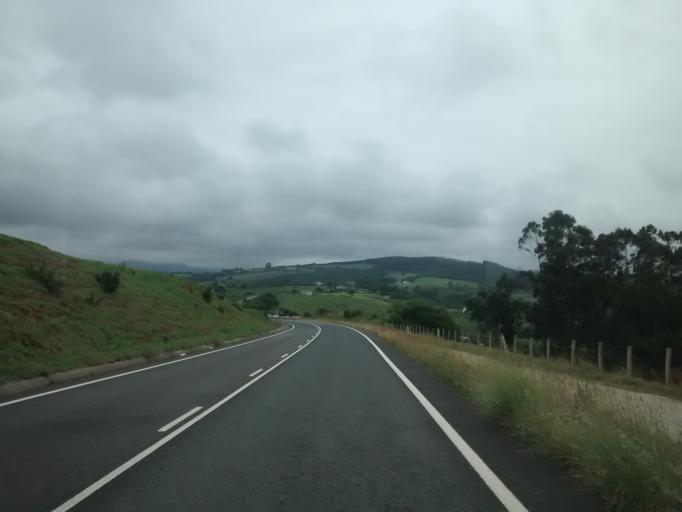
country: ES
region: Cantabria
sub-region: Provincia de Cantabria
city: Santillana
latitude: 43.3992
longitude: -4.1119
